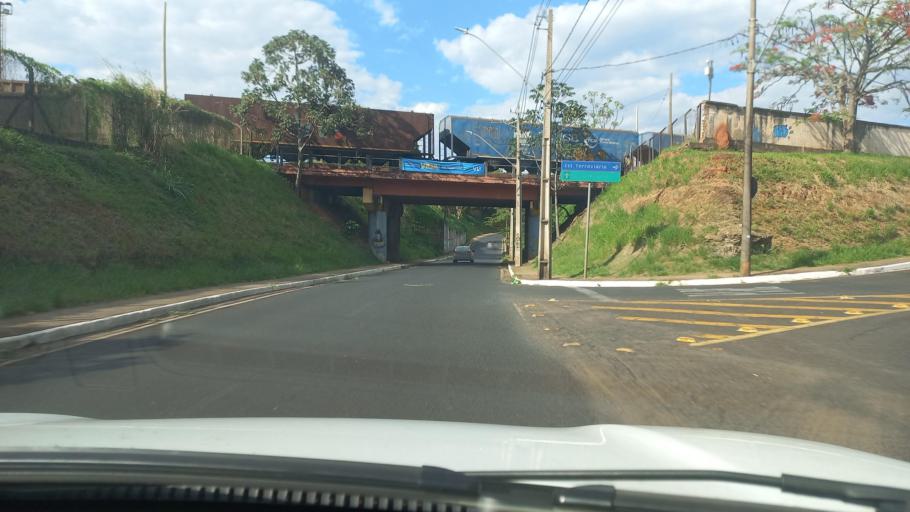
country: BR
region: Minas Gerais
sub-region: Uberaba
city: Uberaba
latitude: -19.7373
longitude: -47.9270
